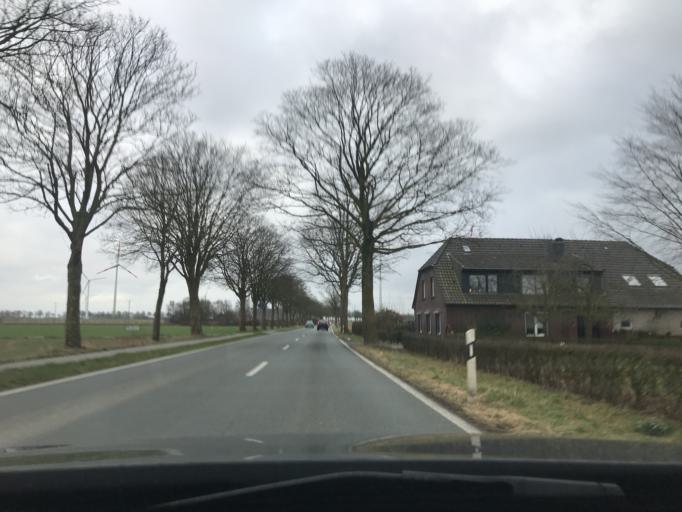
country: DE
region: North Rhine-Westphalia
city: Kalkar
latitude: 51.7166
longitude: 6.2251
